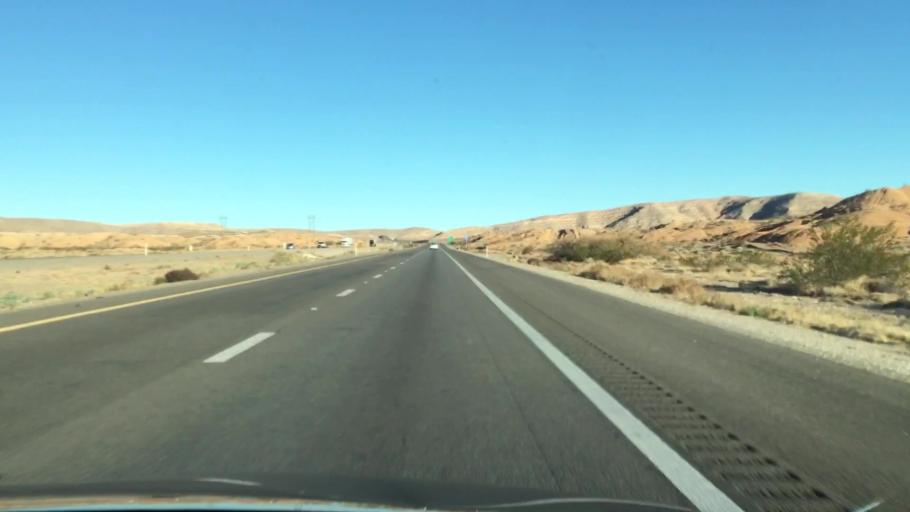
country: US
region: Nevada
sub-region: Clark County
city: Moapa Town
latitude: 36.6659
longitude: -114.5528
